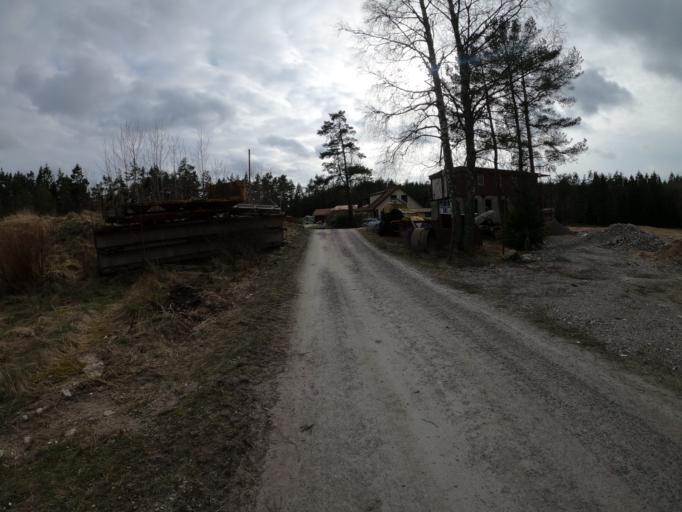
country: SE
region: Vaestra Goetaland
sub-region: Molndal
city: Kallered
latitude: 57.6259
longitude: 12.0767
